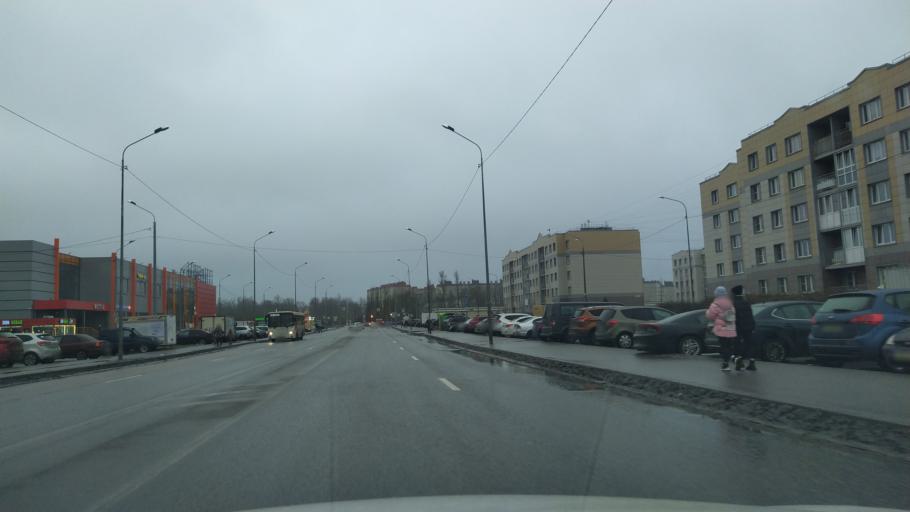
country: RU
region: St.-Petersburg
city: Tyarlevo
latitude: 59.7362
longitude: 30.4688
